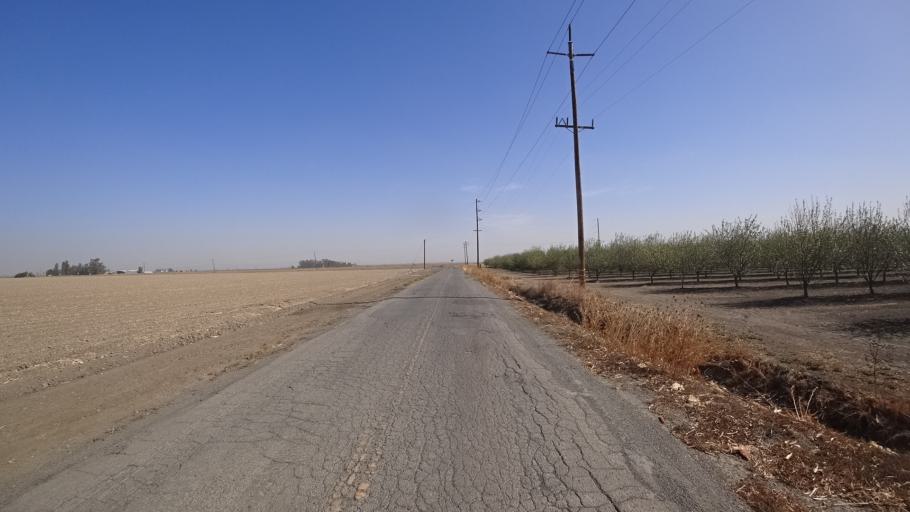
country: US
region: California
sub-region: Yolo County
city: Davis
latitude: 38.5678
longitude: -121.6870
